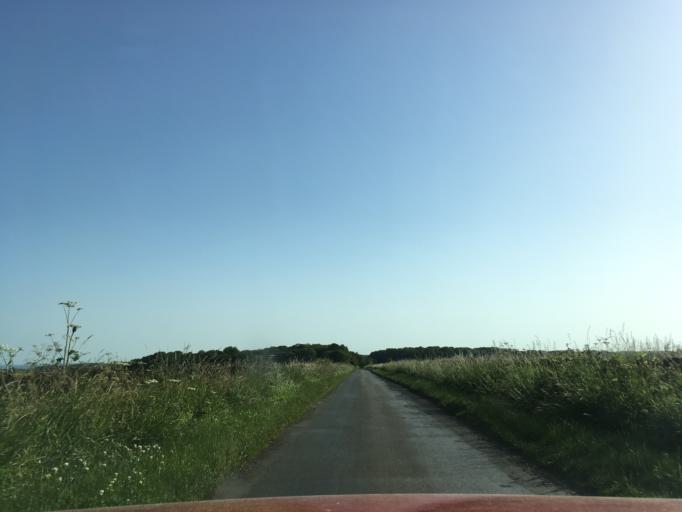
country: GB
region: England
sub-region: Gloucestershire
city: Lechlade
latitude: 51.7713
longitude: -1.7088
